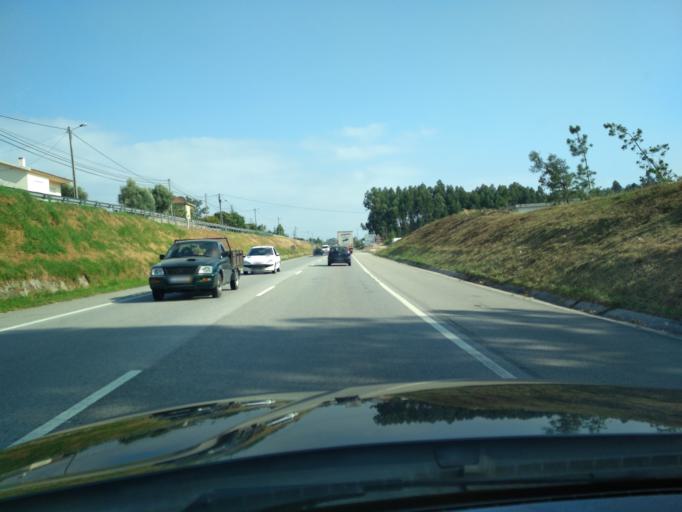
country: PT
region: Aveiro
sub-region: Mealhada
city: Pampilhosa do Botao
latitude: 40.3157
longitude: -8.4514
